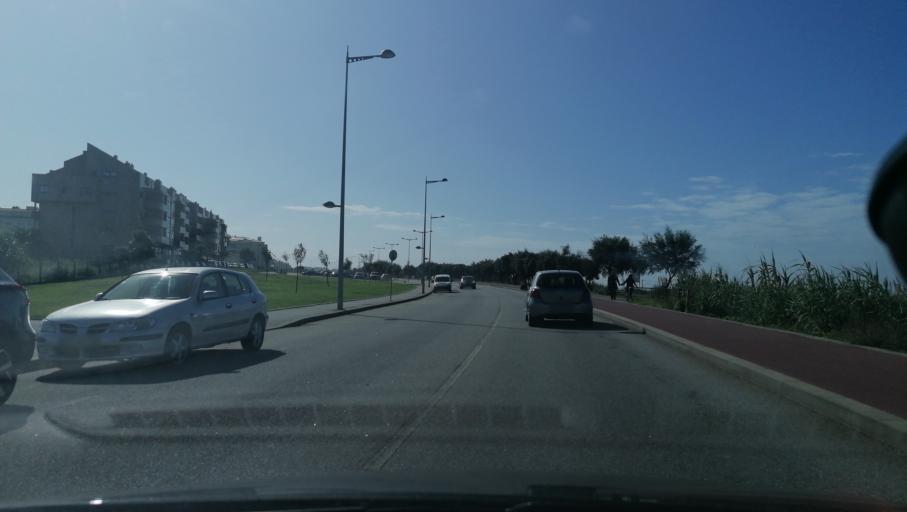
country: PT
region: Aveiro
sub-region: Espinho
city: Espinho
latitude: 41.0260
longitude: -8.6429
